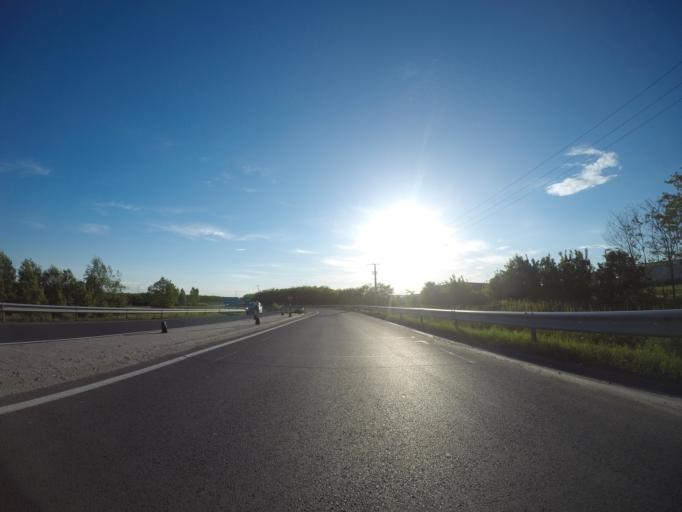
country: HU
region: Pest
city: Nagytarcsa
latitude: 47.5106
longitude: 19.2840
